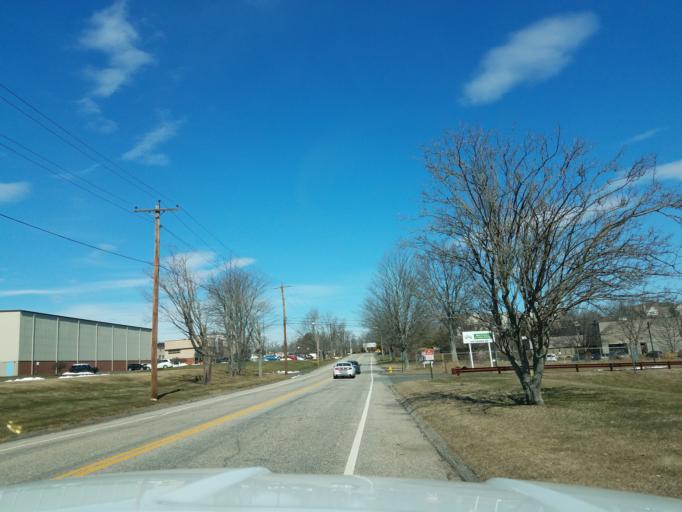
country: US
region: Connecticut
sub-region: New Haven County
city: Orange
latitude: 41.2622
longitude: -72.9965
